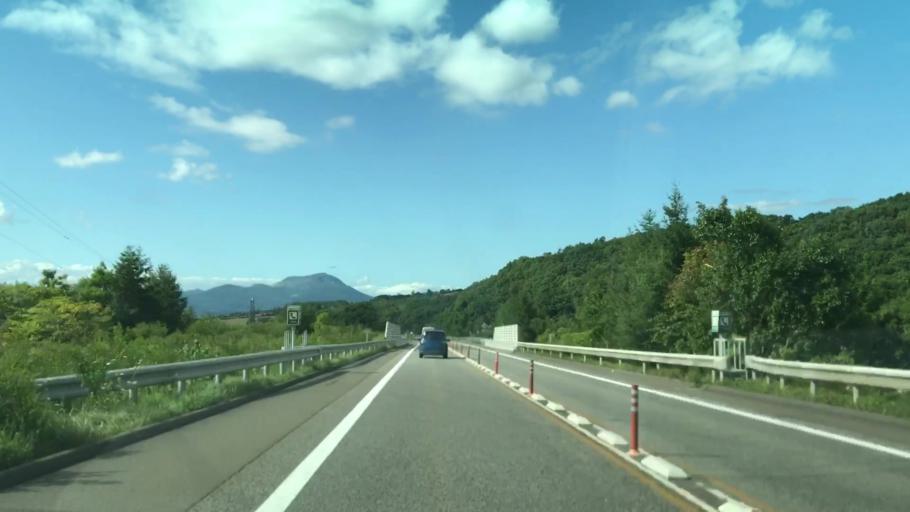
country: JP
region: Hokkaido
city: Date
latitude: 42.4270
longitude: 140.9271
